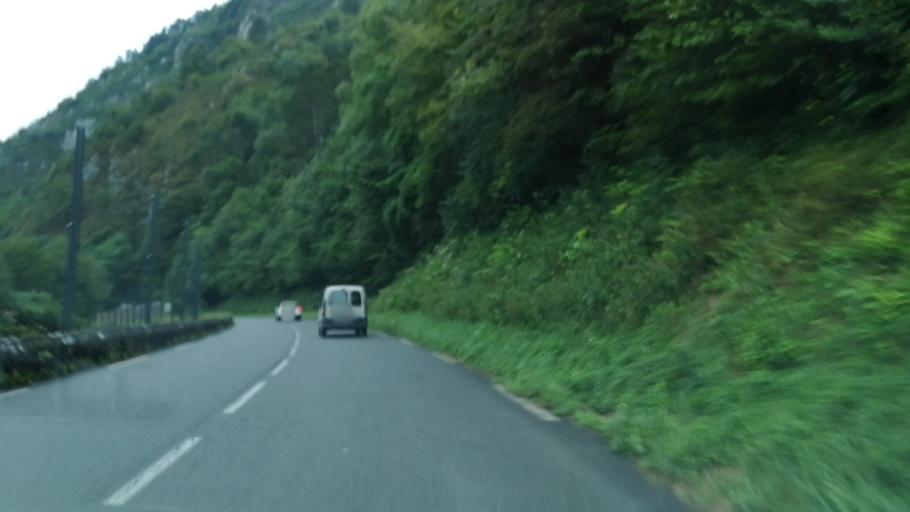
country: FR
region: Aquitaine
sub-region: Departement des Pyrenees-Atlantiques
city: Arette
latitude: 43.0222
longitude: -0.6017
